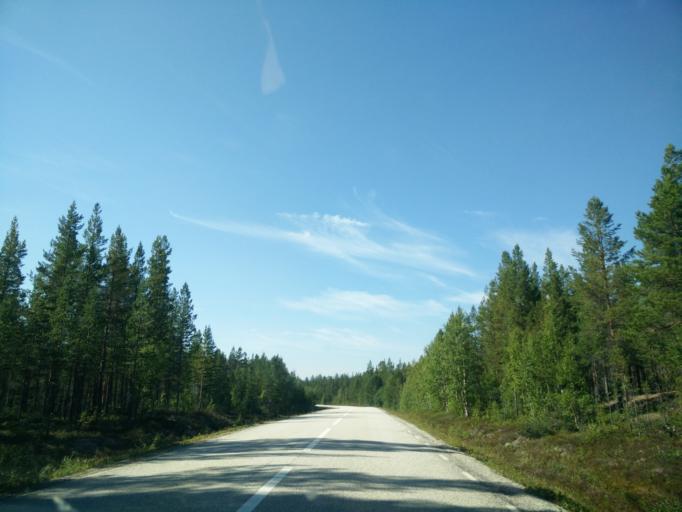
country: SE
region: Jaemtland
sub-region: Are Kommun
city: Jarpen
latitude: 62.8279
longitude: 13.4638
